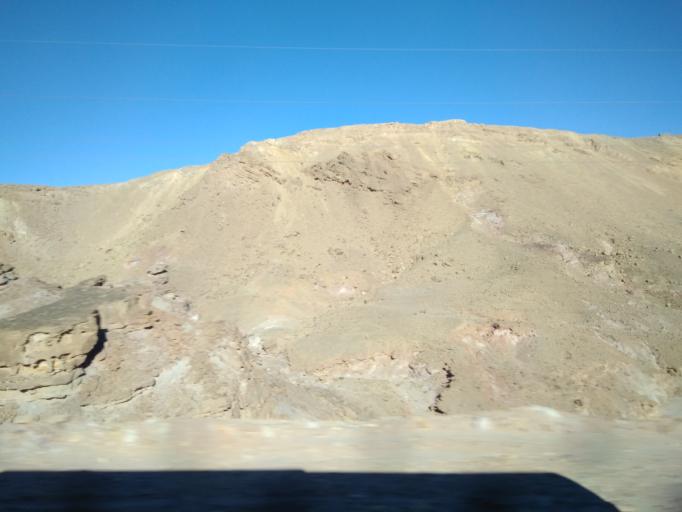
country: IL
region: Southern District
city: Eilat
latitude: 29.6906
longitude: 34.8586
